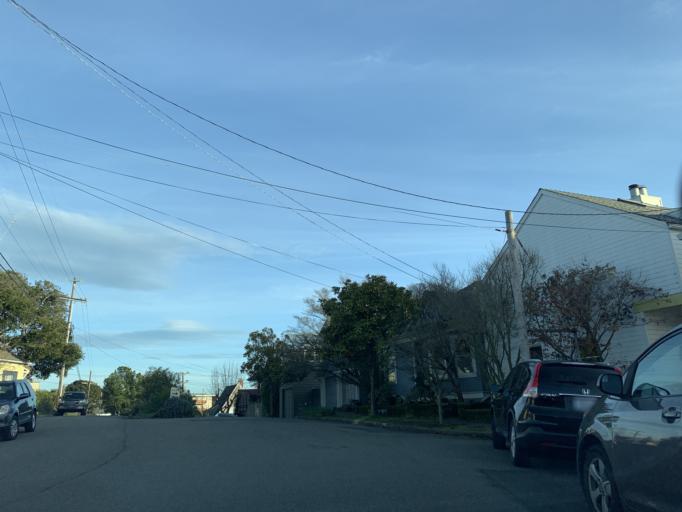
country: US
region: California
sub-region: Contra Costa County
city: North Richmond
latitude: 37.9285
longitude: -122.3919
